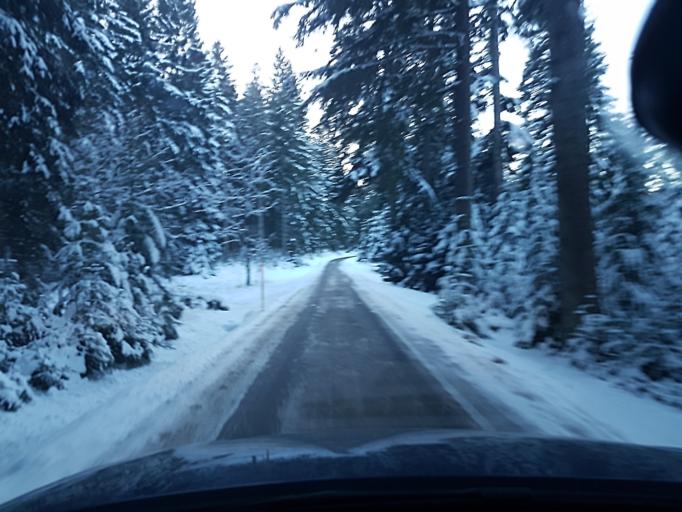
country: DE
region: Baden-Wuerttemberg
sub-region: Freiburg Region
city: Unterkirnach
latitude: 48.0940
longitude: 8.3680
